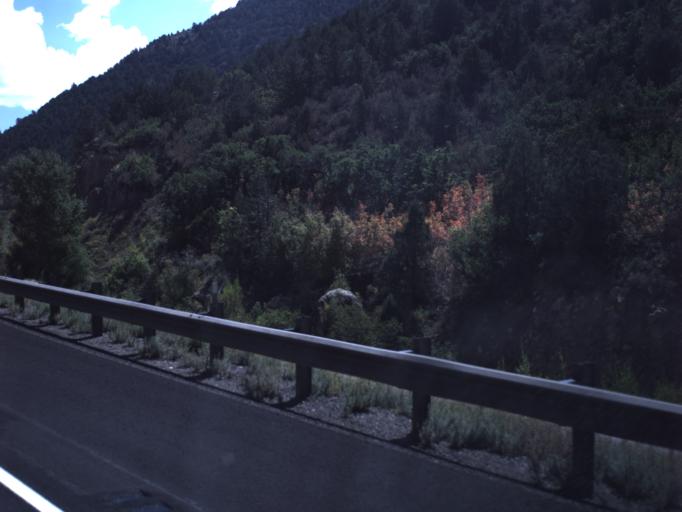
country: US
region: Utah
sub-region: Sevier County
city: Salina
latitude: 38.8953
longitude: -111.6265
